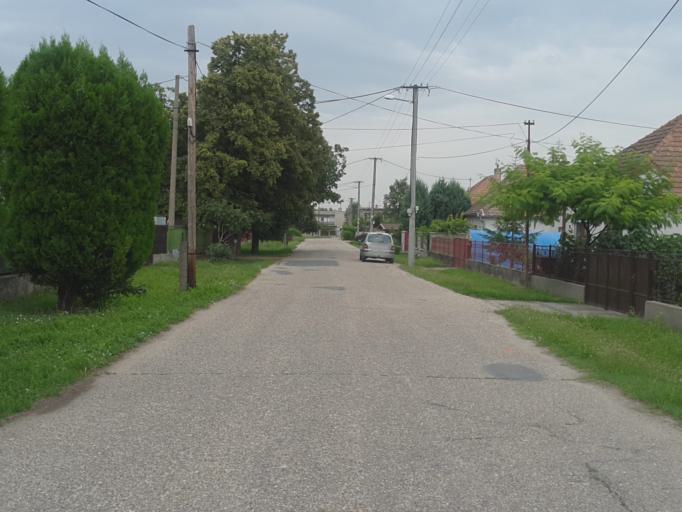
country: SK
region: Nitriansky
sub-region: Okres Komarno
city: Hurbanovo
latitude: 47.8660
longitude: 18.1912
